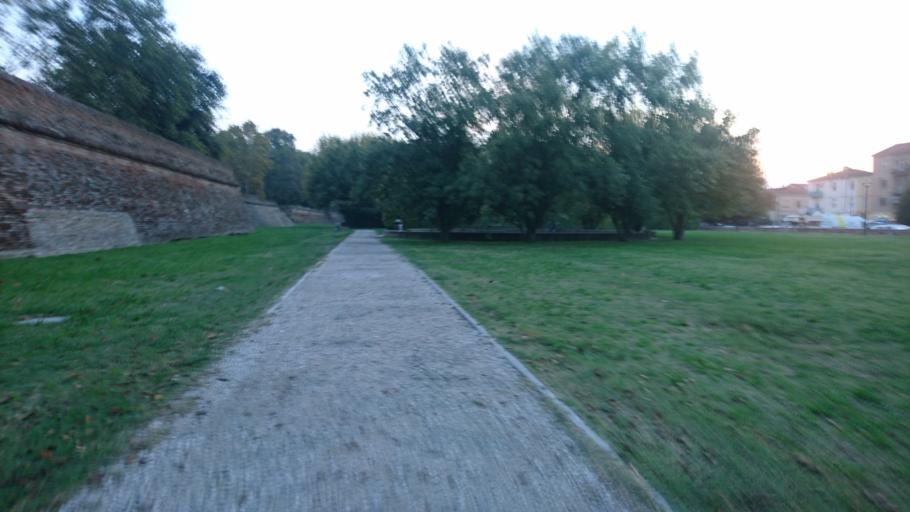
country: IT
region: Emilia-Romagna
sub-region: Provincia di Ferrara
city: Ferrara
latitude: 44.8478
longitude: 11.6134
